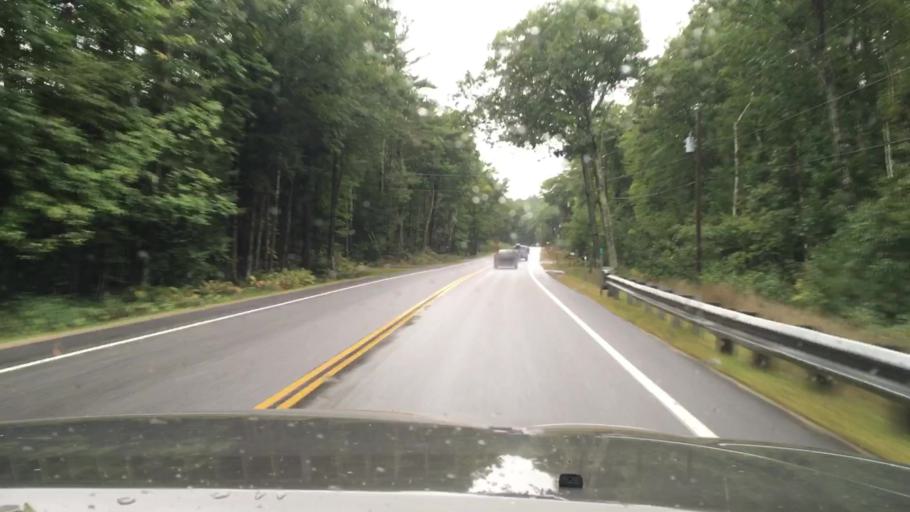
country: US
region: New Hampshire
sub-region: Hillsborough County
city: Antrim
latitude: 43.0760
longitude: -72.0079
